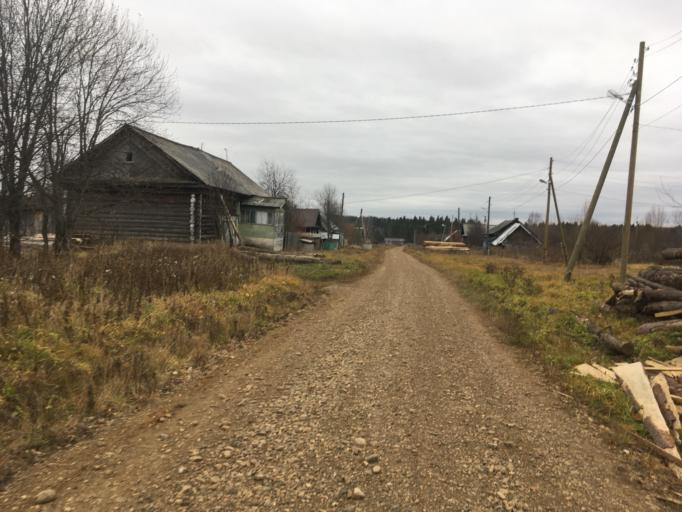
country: RU
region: Perm
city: Komarikhinskiy
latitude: 58.0911
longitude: 57.1112
